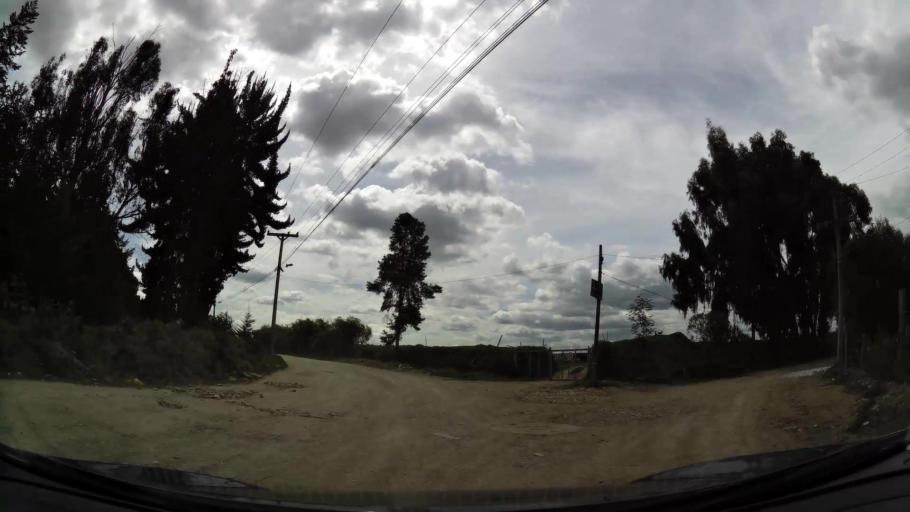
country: CO
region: Cundinamarca
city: Funza
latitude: 4.7323
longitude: -74.1518
